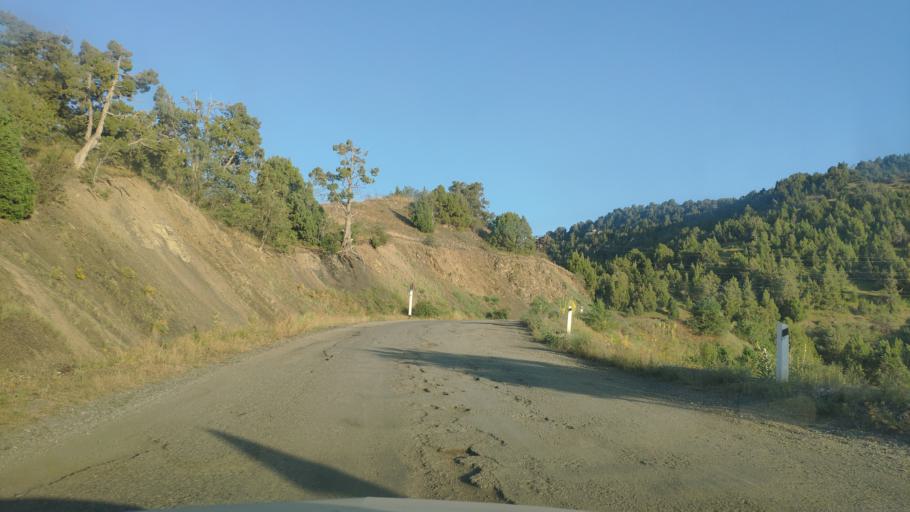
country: TJ
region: Viloyati Sughd
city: Ayni
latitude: 39.6413
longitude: 68.4696
